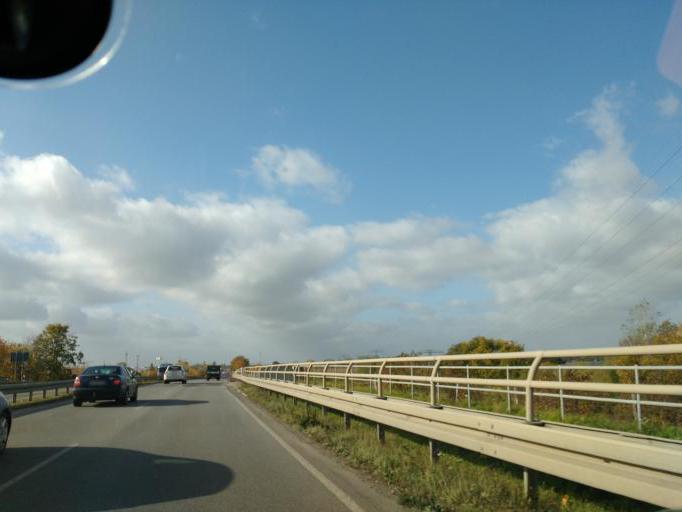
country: DE
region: Brandenburg
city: Petershagen
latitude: 52.4944
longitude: 13.7750
